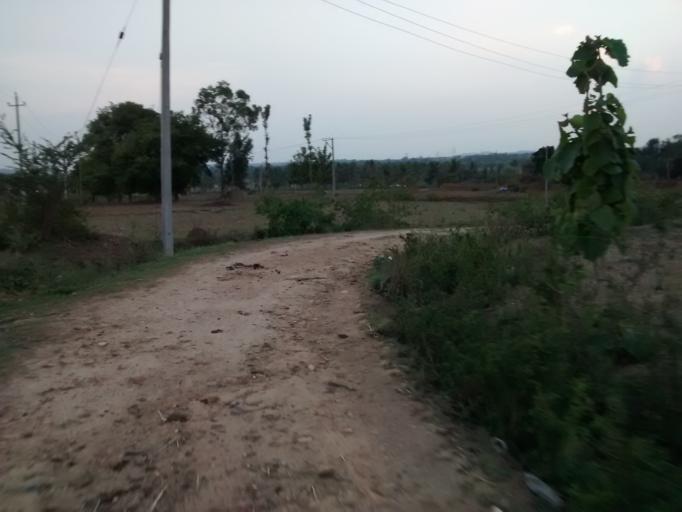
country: IN
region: Karnataka
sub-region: Hassan
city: Hassan
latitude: 12.9399
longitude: 76.1547
